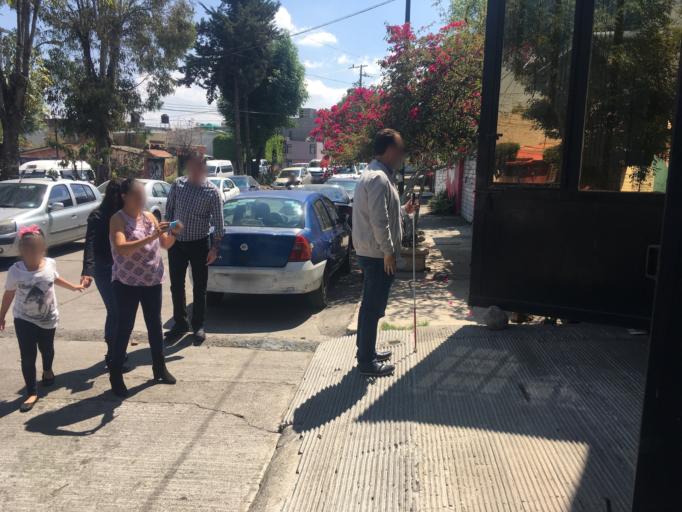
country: MX
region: Michoacan
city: Morelia
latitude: 19.7086
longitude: -101.2180
